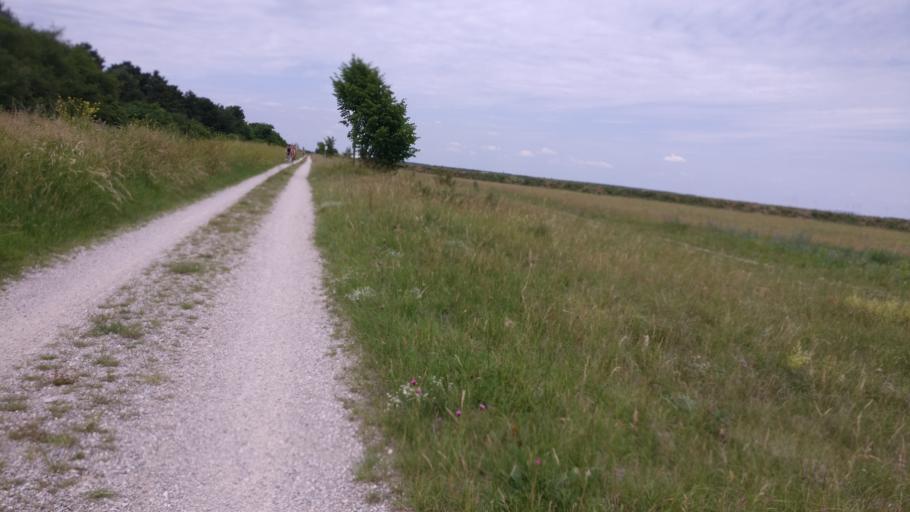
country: AT
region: Lower Austria
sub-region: Politischer Bezirk Wiener Neustadt
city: Sollenau
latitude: 47.8692
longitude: 16.2816
